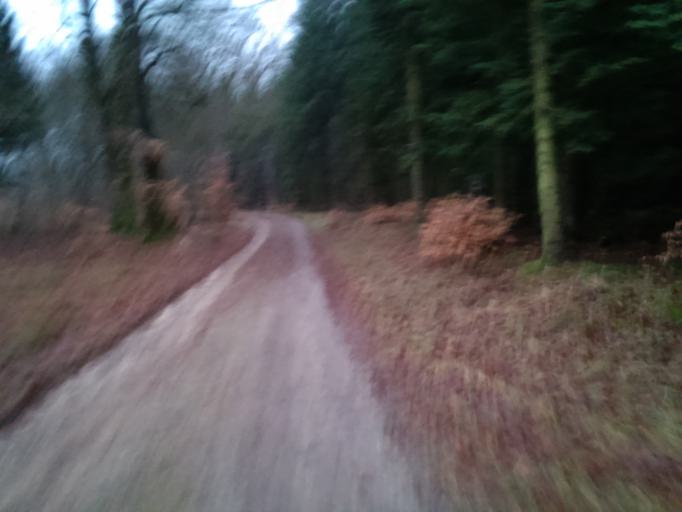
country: DK
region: North Denmark
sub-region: Mariagerfjord Kommune
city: Arden
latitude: 56.7915
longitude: 9.7565
